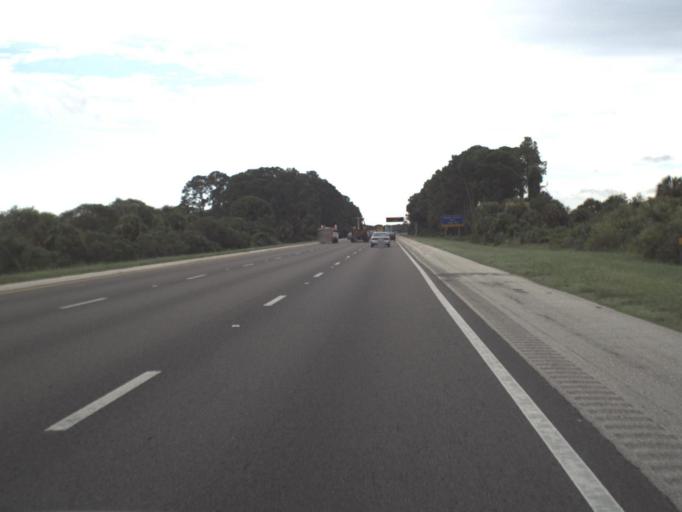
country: US
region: Florida
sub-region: Sarasota County
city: Osprey
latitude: 27.2191
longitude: -82.4484
